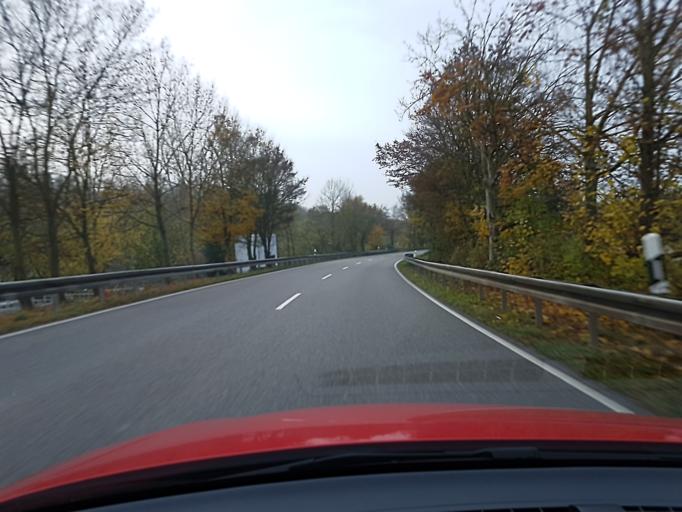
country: DE
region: Baden-Wuerttemberg
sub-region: Regierungsbezirk Stuttgart
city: Walheim
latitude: 49.0120
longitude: 9.1583
